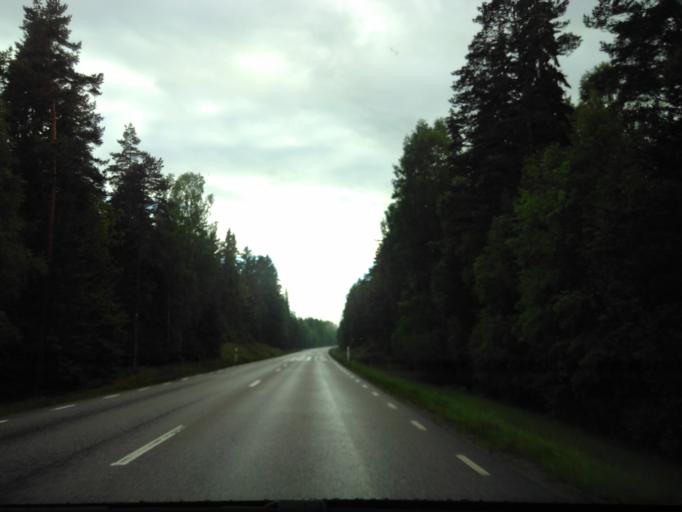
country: SE
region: Vaestra Goetaland
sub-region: Falkopings Kommun
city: Floby
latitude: 58.1063
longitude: 13.1840
